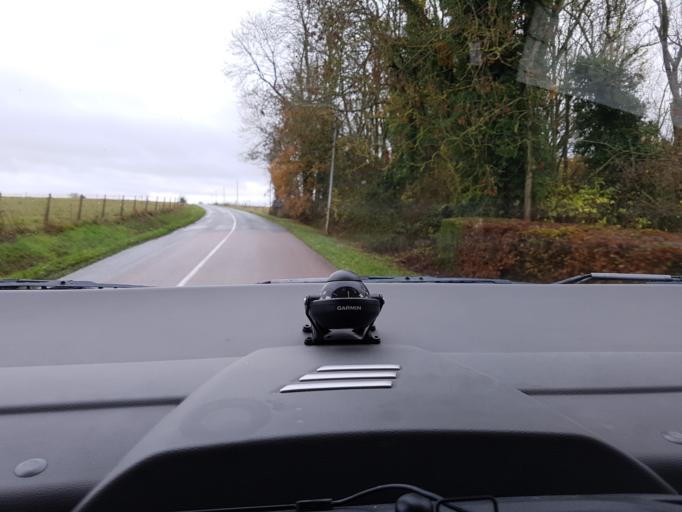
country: FR
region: Haute-Normandie
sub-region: Departement de l'Eure
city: Pont-Saint-Pierre
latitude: 49.3114
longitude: 1.3110
